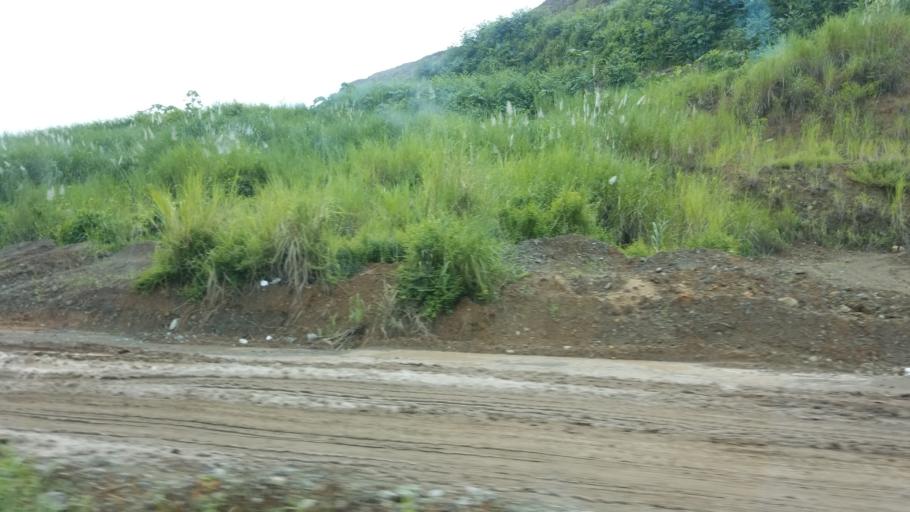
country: PA
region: Panama
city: San Miguelito
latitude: 9.0997
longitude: -79.4744
